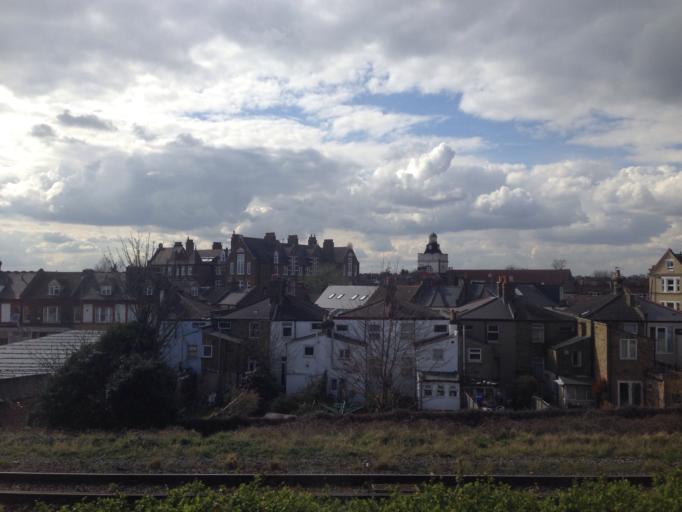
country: GB
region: England
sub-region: Greater London
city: Brixton Hill
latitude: 51.4214
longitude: -0.1382
